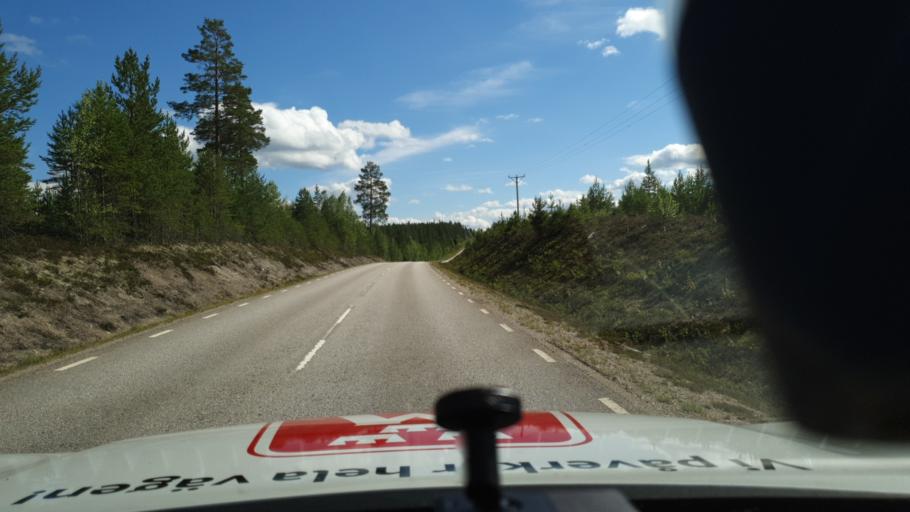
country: NO
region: Hedmark
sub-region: Trysil
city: Innbygda
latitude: 60.9917
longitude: 12.4923
